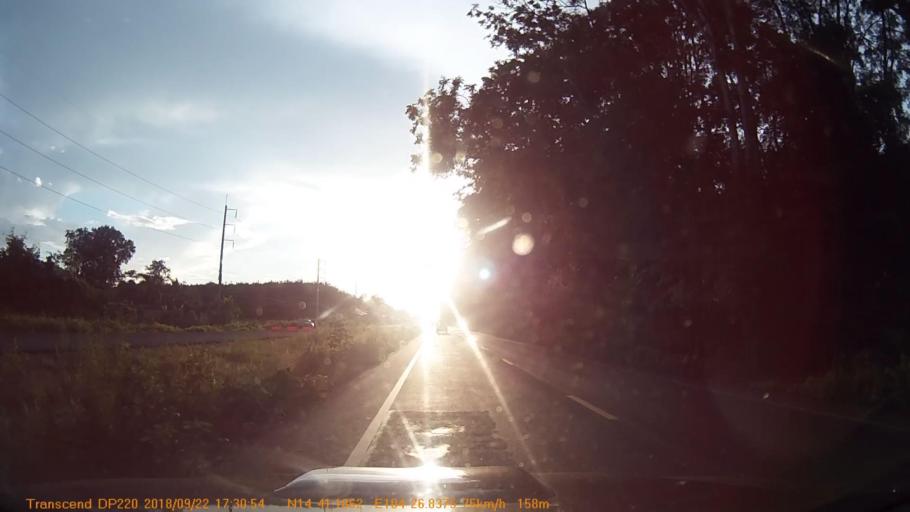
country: TH
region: Sisaket
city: Khun Han
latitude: 14.6864
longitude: 104.4467
